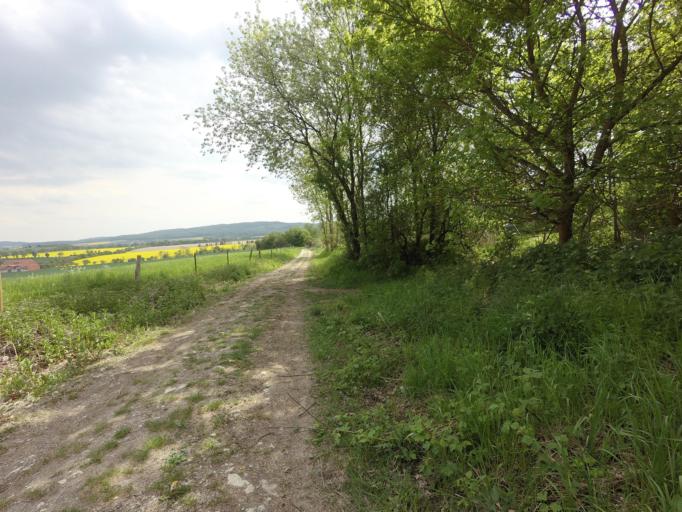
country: DE
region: Lower Saxony
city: Diekholzen
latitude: 52.1180
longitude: 9.9158
